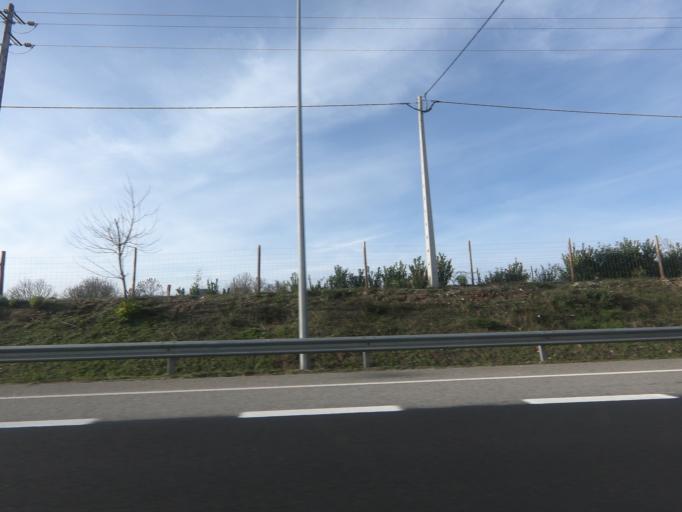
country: PT
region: Viseu
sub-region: Concelho de Tondela
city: Tondela
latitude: 40.5252
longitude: -8.0894
